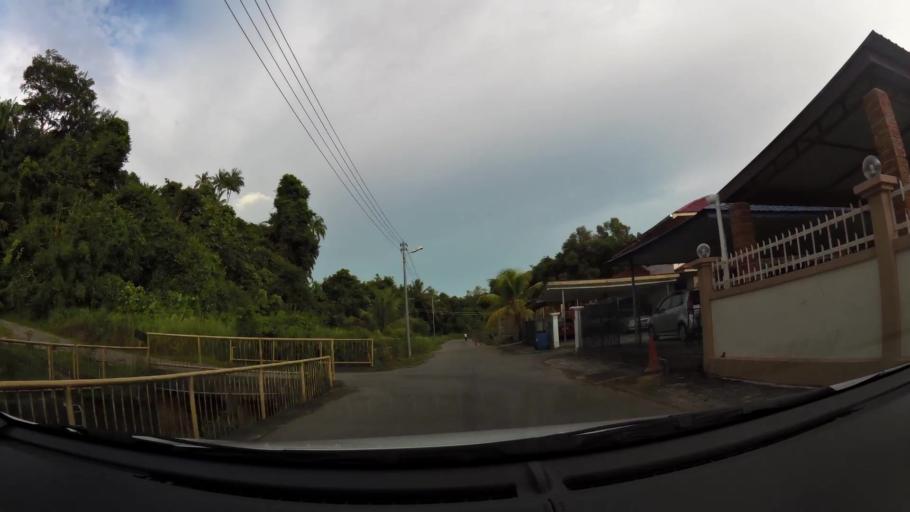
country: BN
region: Brunei and Muara
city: Bandar Seri Begawan
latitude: 4.9743
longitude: 114.9866
